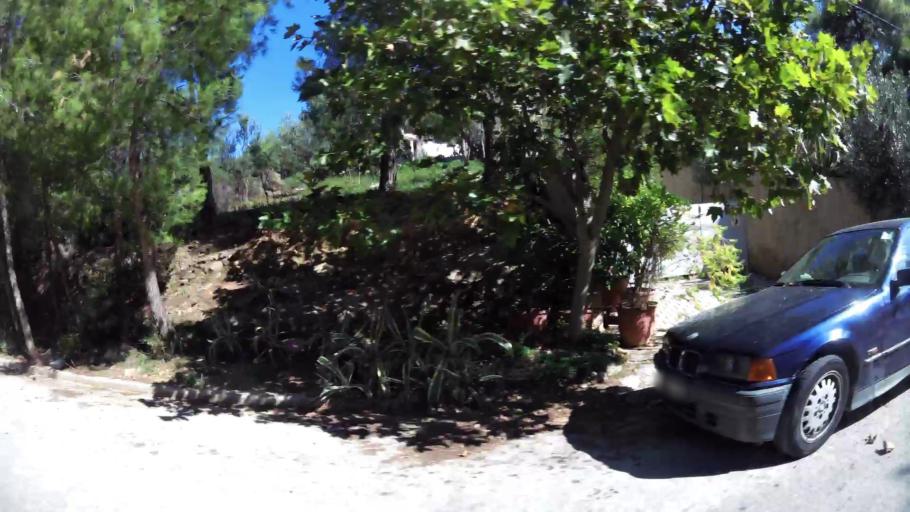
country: GR
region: Attica
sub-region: Nomarchia Anatolikis Attikis
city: Dioni
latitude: 38.0262
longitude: 23.9346
